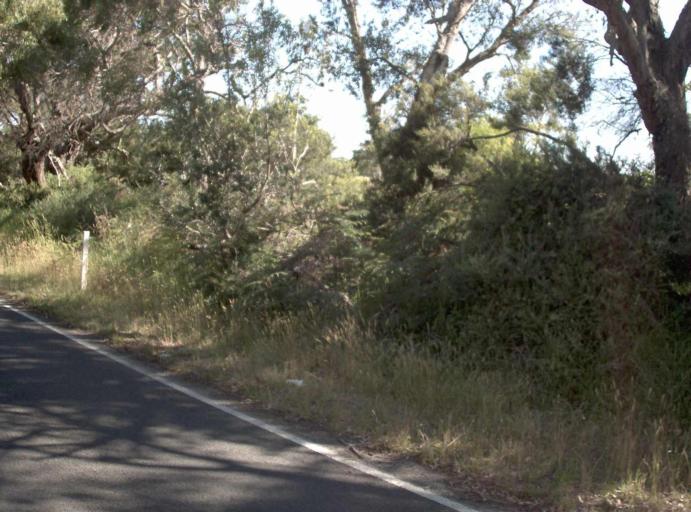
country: AU
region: Victoria
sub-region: Latrobe
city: Traralgon
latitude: -38.6622
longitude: 146.6851
